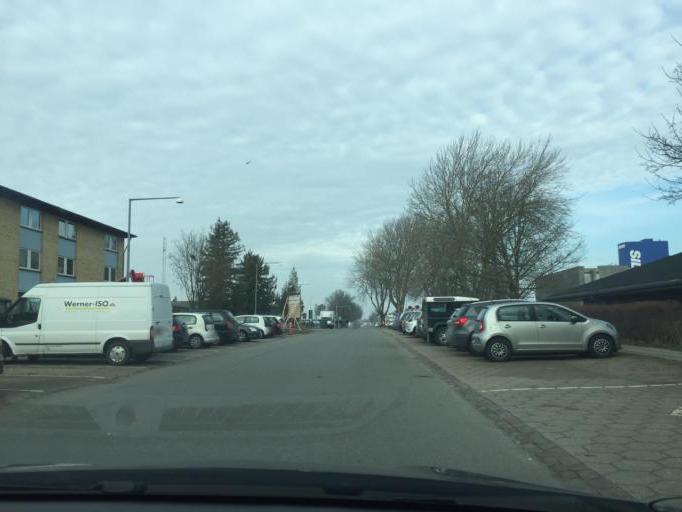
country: DK
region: South Denmark
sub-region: Odense Kommune
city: Neder Holluf
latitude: 55.3779
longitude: 10.4242
